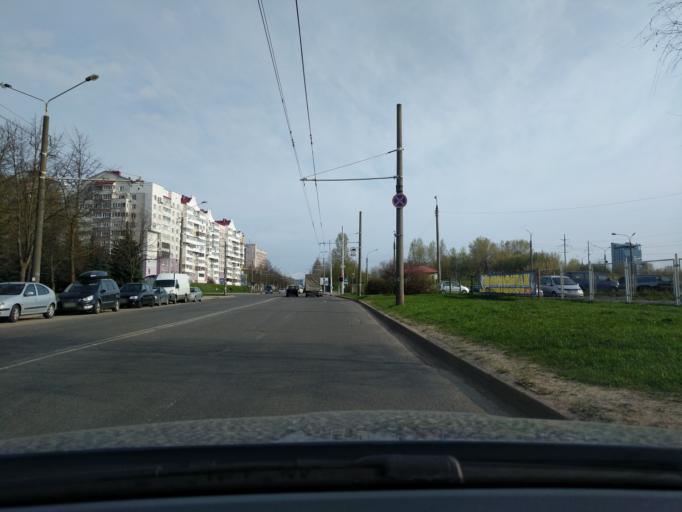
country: BY
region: Minsk
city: Novoye Medvezhino
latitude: 53.9029
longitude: 27.4632
